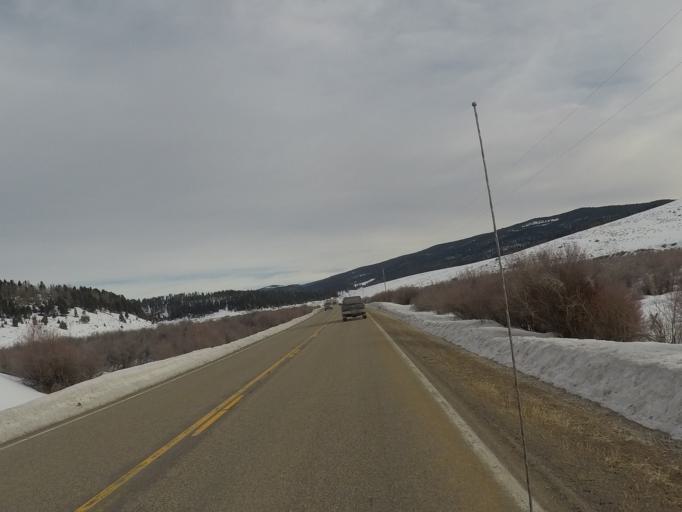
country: US
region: Montana
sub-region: Meagher County
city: White Sulphur Springs
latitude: 46.7160
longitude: -110.8581
